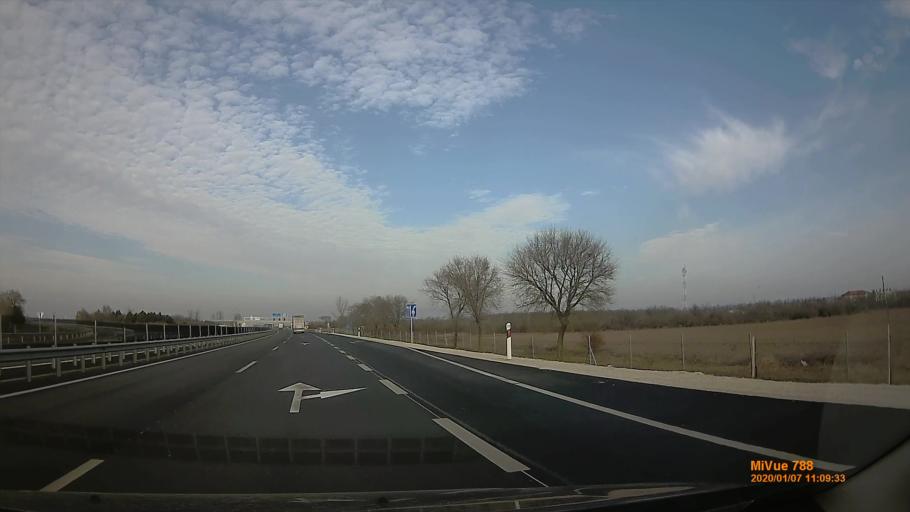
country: HU
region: Gyor-Moson-Sopron
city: Rajka
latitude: 47.9988
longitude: 17.1849
